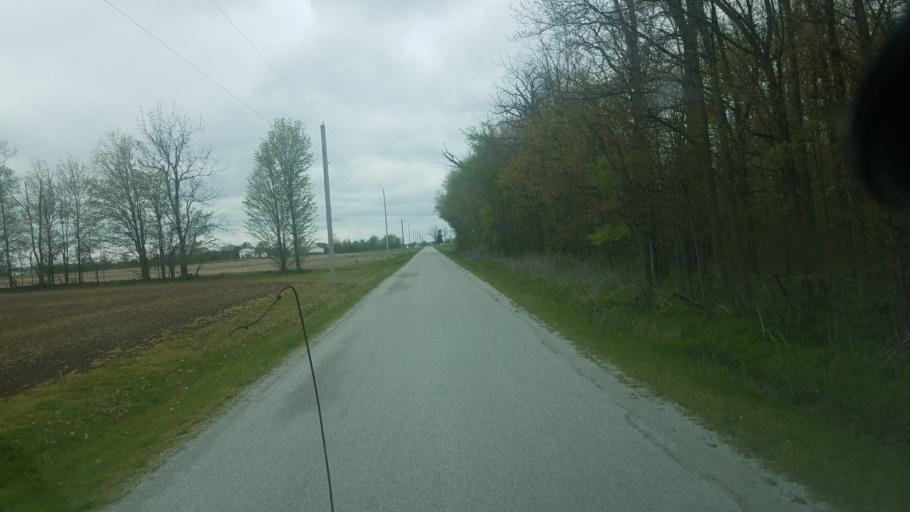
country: US
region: Ohio
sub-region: Hardin County
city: Forest
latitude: 40.7238
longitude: -83.5524
